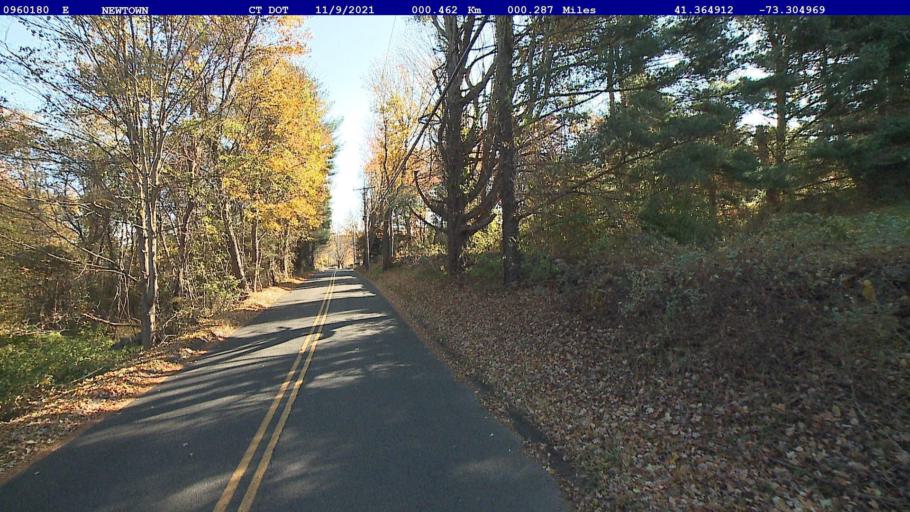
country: US
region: Connecticut
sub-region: Fairfield County
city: Newtown
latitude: 41.3648
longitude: -73.3050
